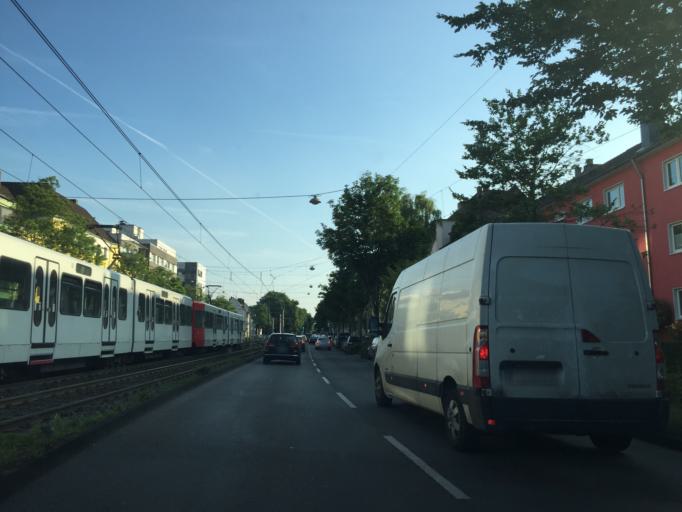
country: DE
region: North Rhine-Westphalia
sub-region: Regierungsbezirk Koln
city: Neustadt/Sued
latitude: 50.9077
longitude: 6.9189
